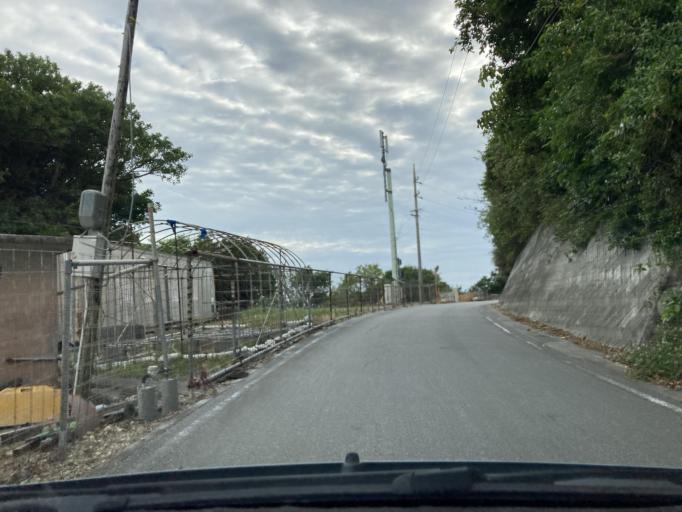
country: JP
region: Okinawa
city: Tomigusuku
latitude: 26.1356
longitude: 127.7926
